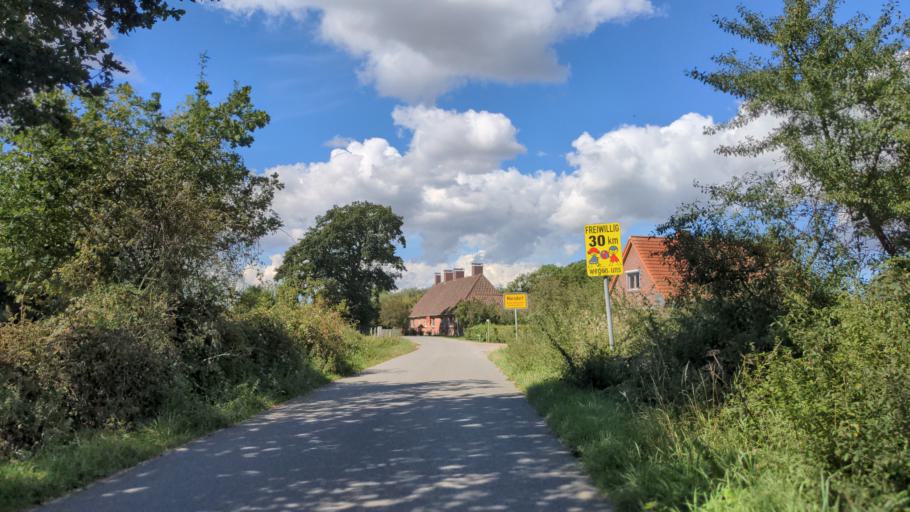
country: DE
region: Schleswig-Holstein
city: Beschendorf
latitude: 54.1755
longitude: 10.8469
